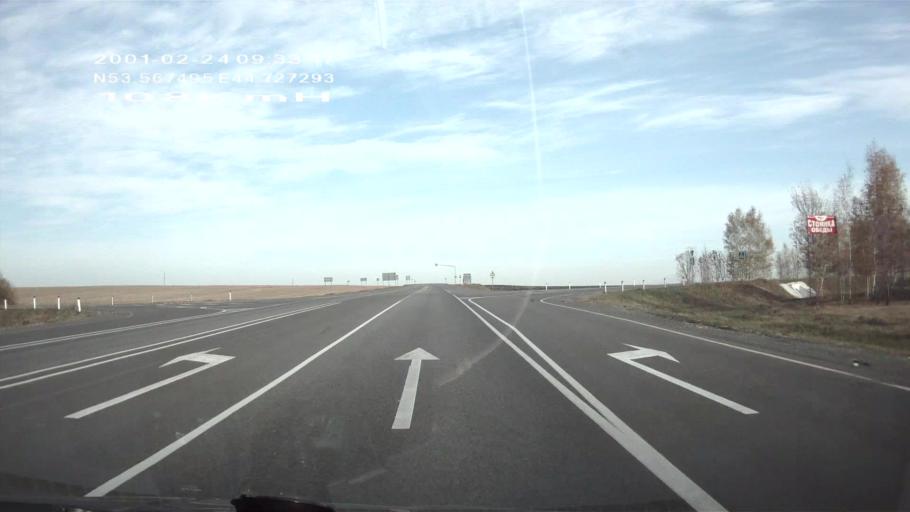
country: RU
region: Penza
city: Mokshan
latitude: 53.5676
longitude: 44.7273
